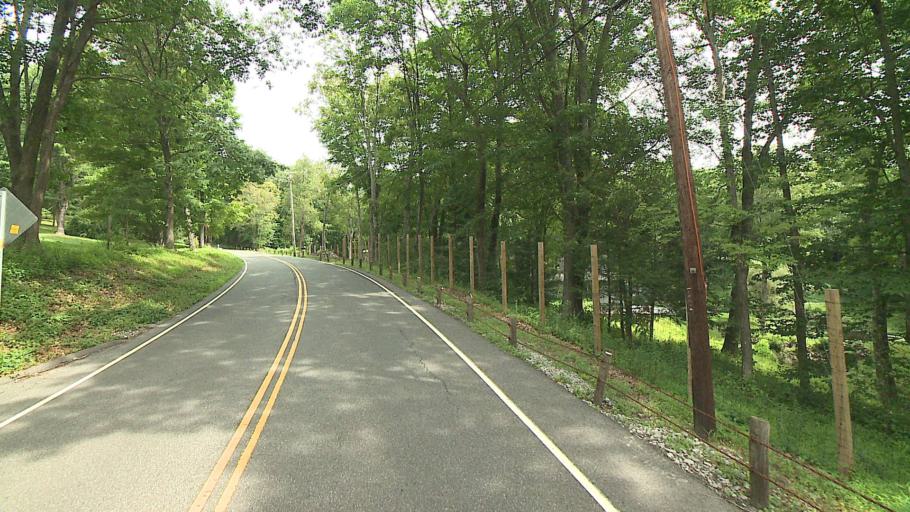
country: US
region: Connecticut
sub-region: Litchfield County
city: New Preston
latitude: 41.5937
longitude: -73.3195
